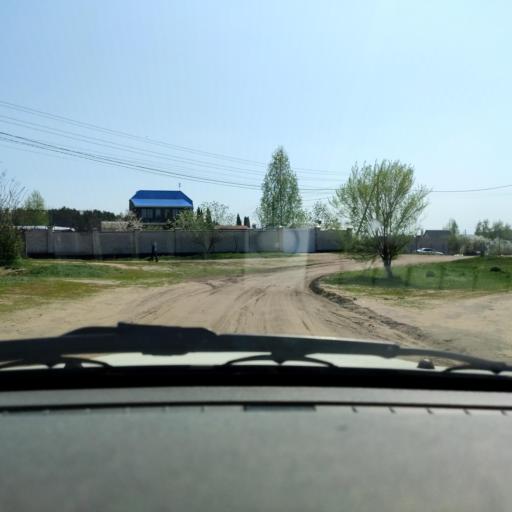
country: RU
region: Voronezj
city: Shilovo
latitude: 51.5625
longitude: 39.0645
